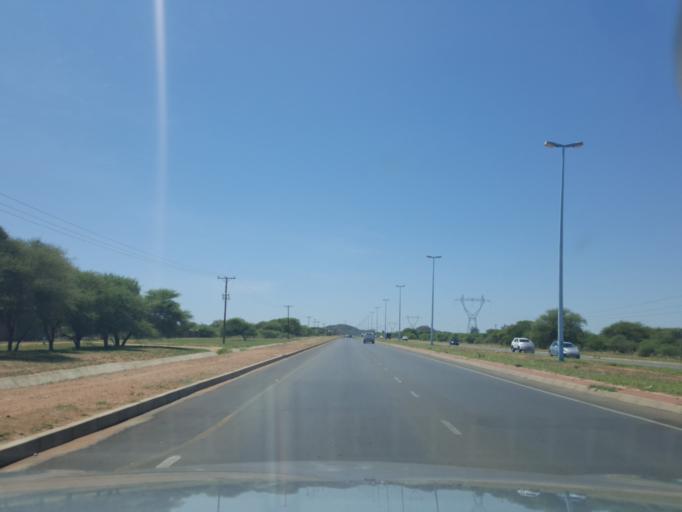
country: BW
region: Kweneng
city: Gaphatshwe
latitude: -24.5810
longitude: 25.8375
